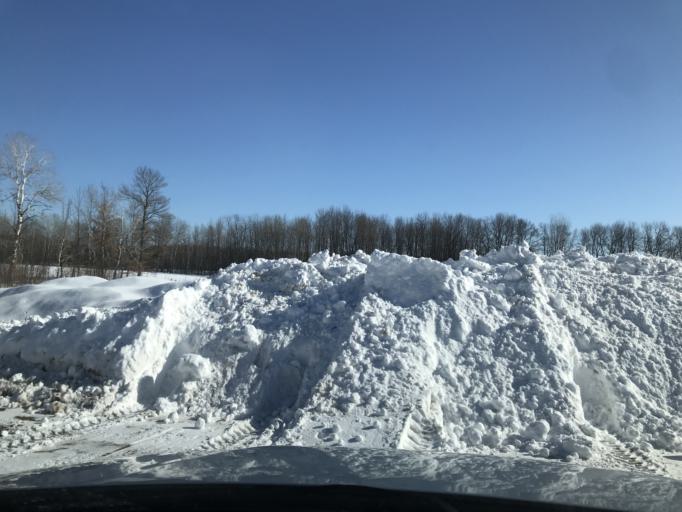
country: US
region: Wisconsin
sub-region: Marinette County
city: Peshtigo
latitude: 45.1714
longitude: -87.7641
